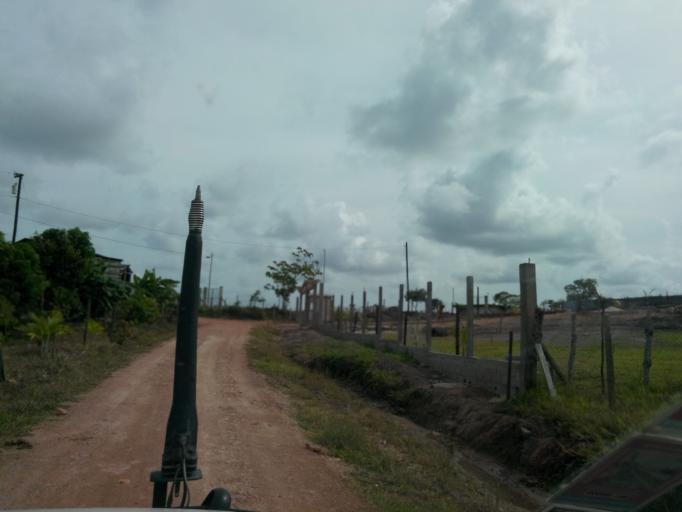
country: NI
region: Atlantico Sur
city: Bluefields
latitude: 11.9944
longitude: -83.7716
